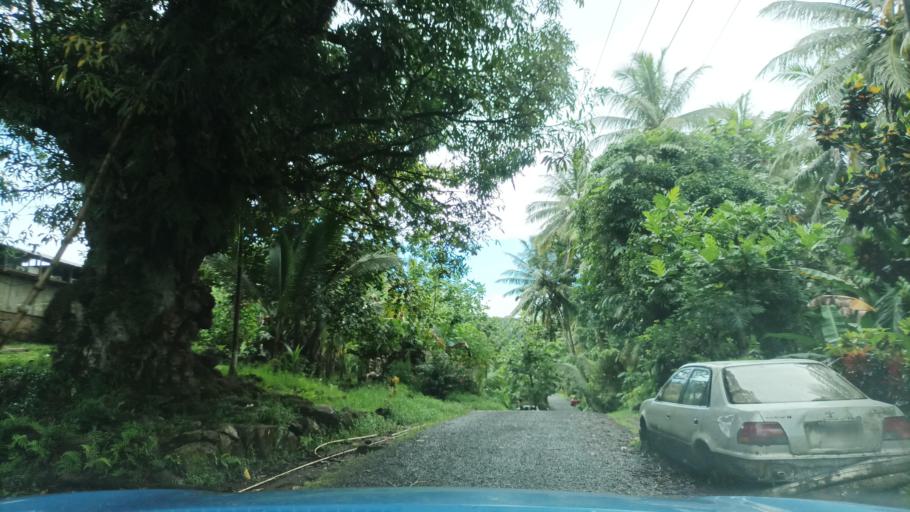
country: FM
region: Pohnpei
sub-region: Sokehs Municipality
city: Palikir - National Government Center
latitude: 6.8335
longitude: 158.1705
